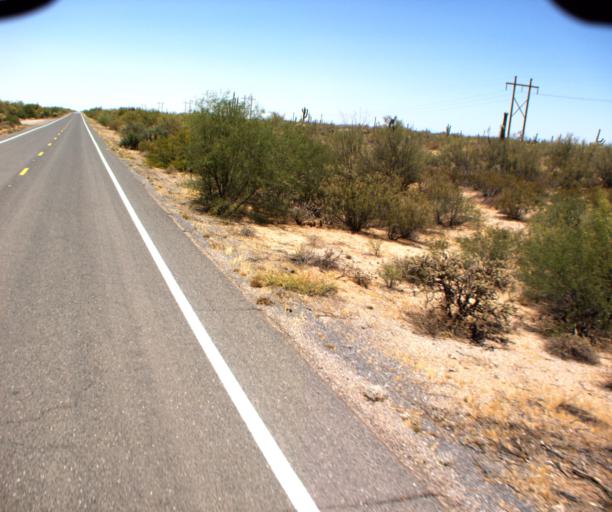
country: US
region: Arizona
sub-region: Pinal County
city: Florence
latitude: 32.8056
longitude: -111.1877
